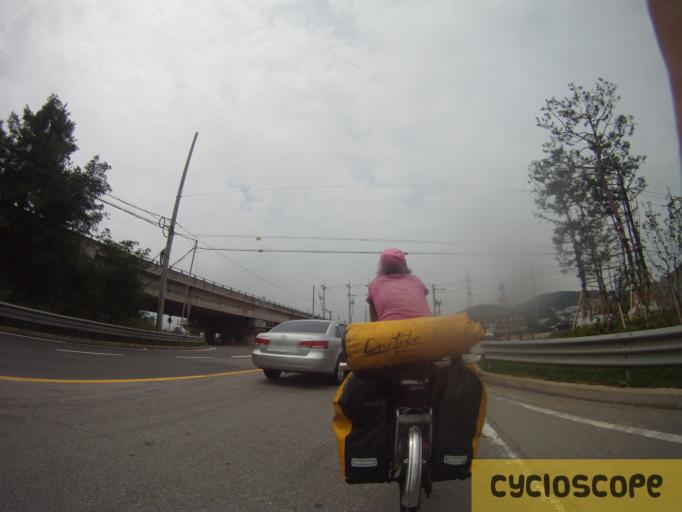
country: KR
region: Gyeonggi-do
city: Hwaseong-si
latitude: 37.1568
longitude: 126.8989
